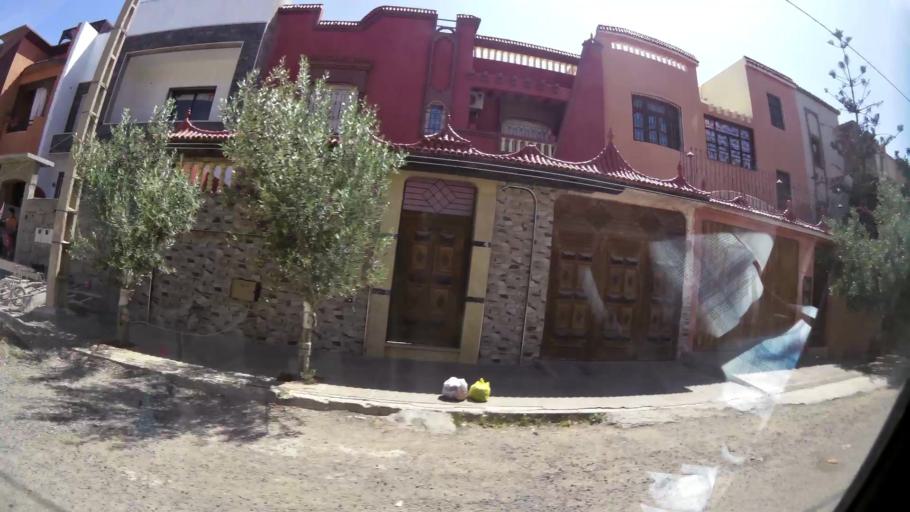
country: MA
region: Souss-Massa-Draa
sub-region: Inezgane-Ait Mellou
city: Inezgane
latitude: 30.3235
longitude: -9.5056
